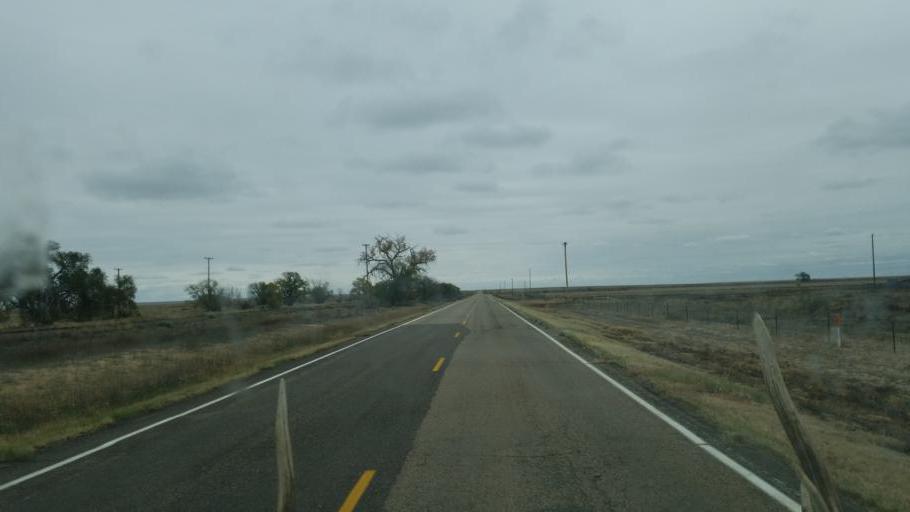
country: US
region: Colorado
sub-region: Crowley County
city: Ordway
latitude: 38.2366
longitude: -103.6485
